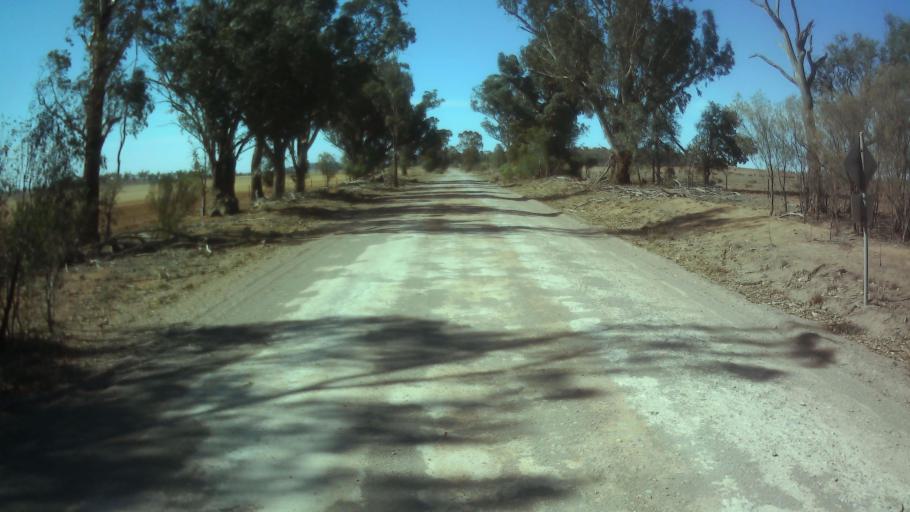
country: AU
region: New South Wales
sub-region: Forbes
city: Forbes
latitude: -33.7207
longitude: 147.7456
